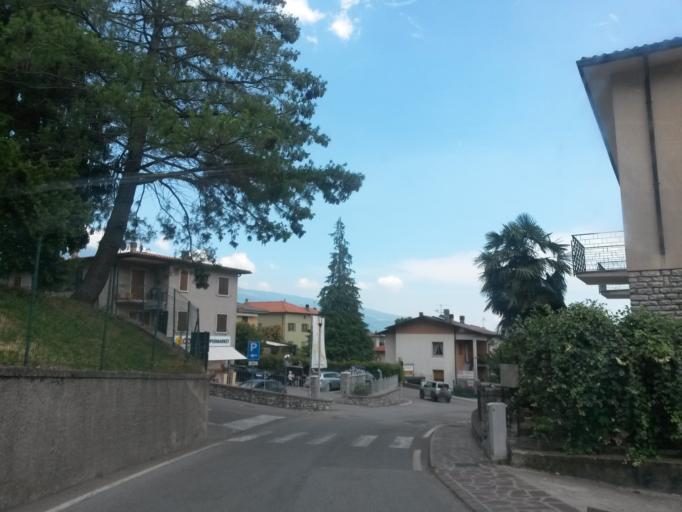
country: IT
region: Lombardy
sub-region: Provincia di Brescia
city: Gardola
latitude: 45.7403
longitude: 10.7205
